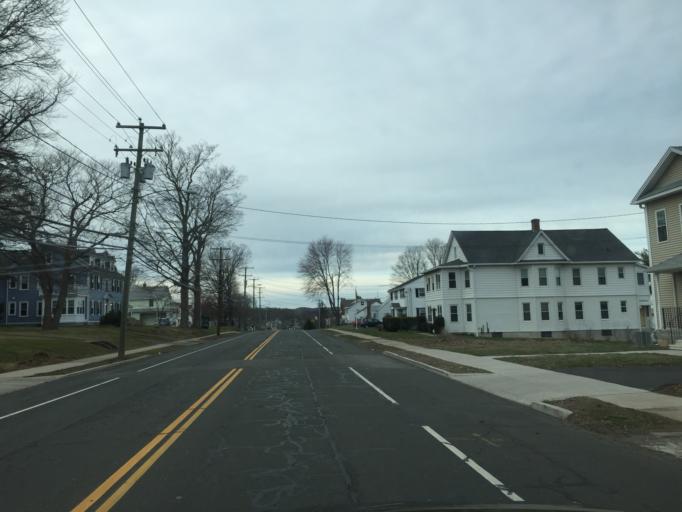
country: US
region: Connecticut
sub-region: Hartford County
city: New Britain
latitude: 41.6897
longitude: -72.7895
